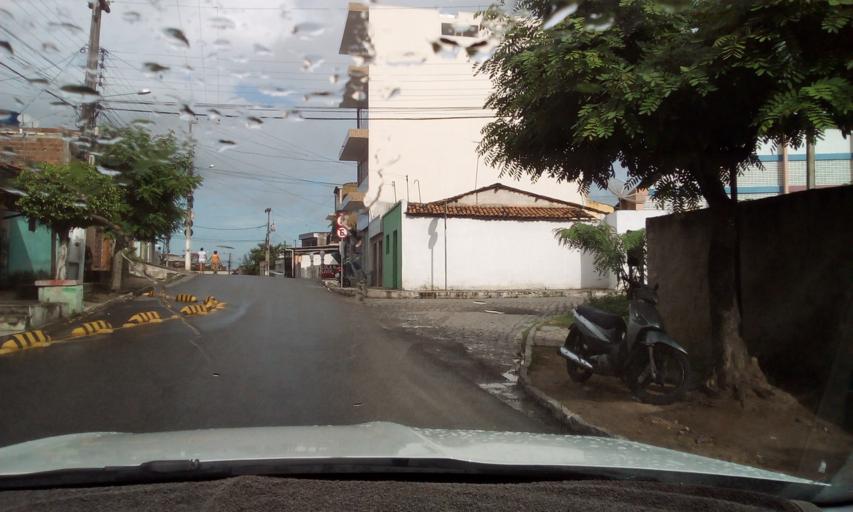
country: BR
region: Paraiba
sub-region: Guarabira
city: Guarabira
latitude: -6.8534
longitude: -35.4976
